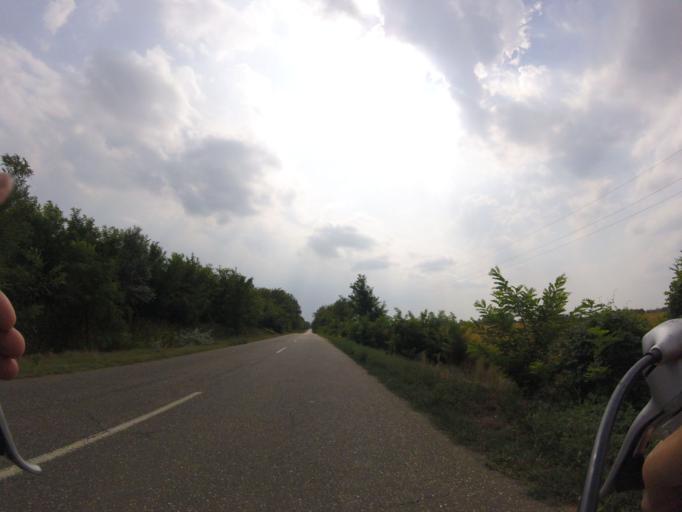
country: HU
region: Szabolcs-Szatmar-Bereg
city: Levelek
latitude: 47.9874
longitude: 21.9687
